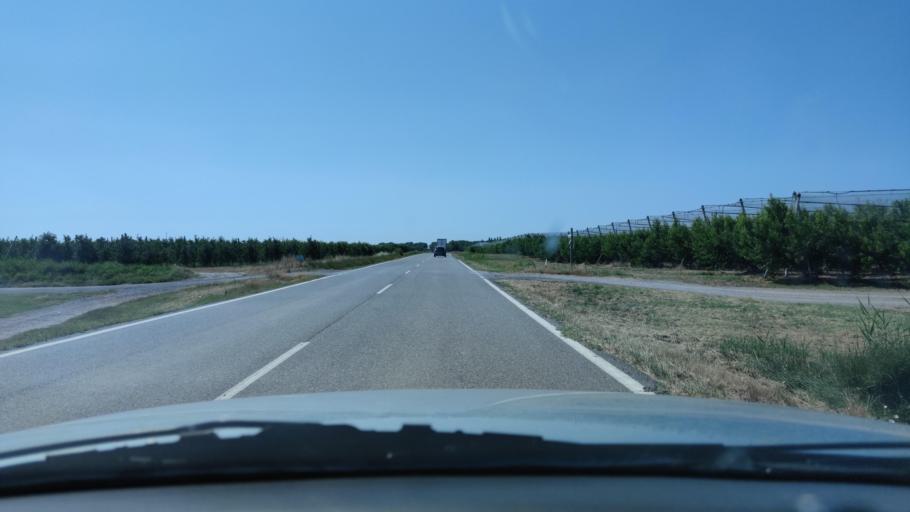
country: ES
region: Catalonia
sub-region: Provincia de Lleida
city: Ivars d'Urgell
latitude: 41.6990
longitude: 0.9833
